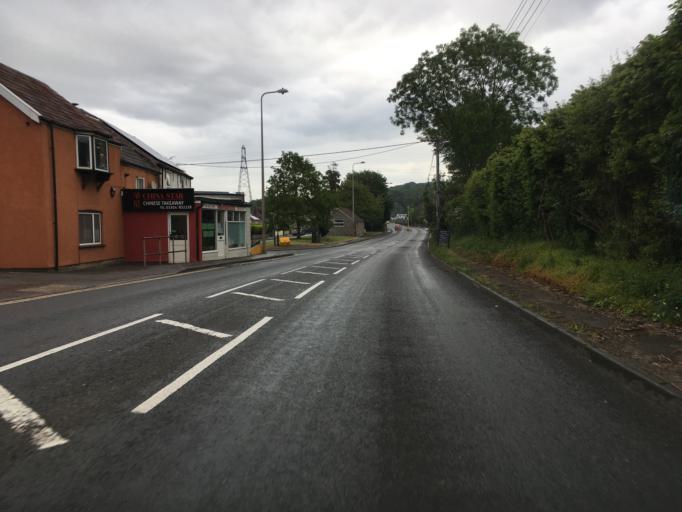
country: GB
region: England
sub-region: North Somerset
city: Brockley
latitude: 51.3857
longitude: -2.7861
